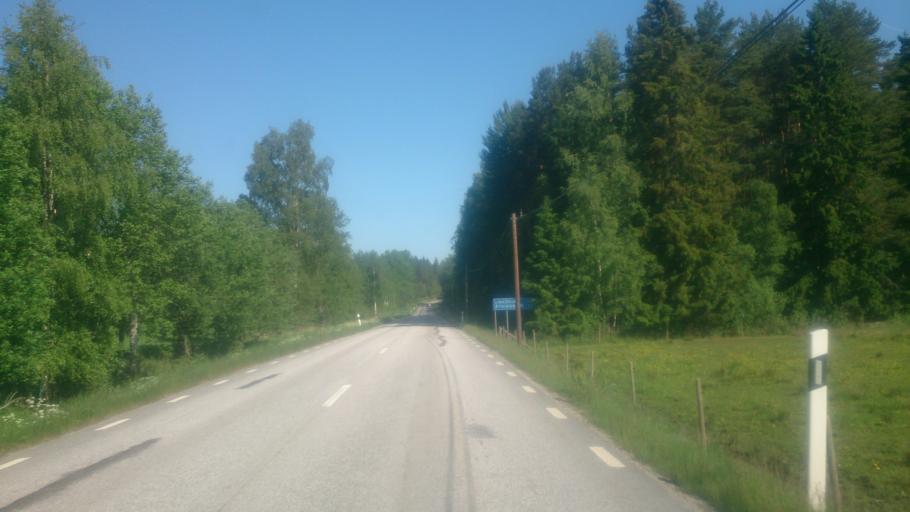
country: SE
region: OEstergoetland
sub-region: Atvidabergs Kommun
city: Atvidaberg
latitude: 58.1185
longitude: 16.0967
